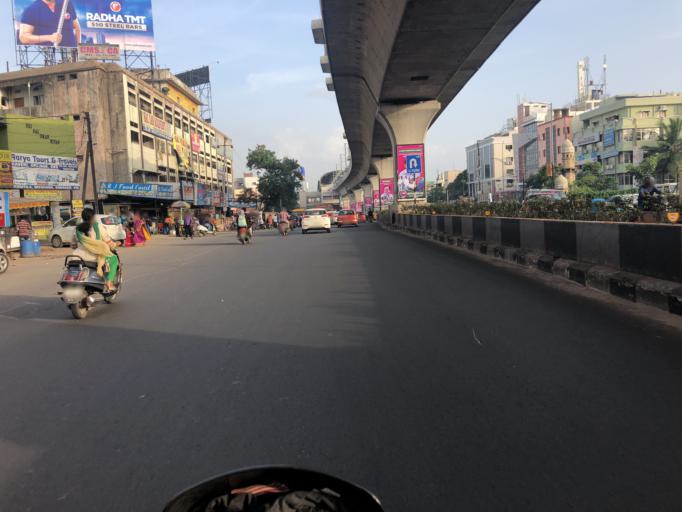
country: IN
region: Telangana
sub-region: Rangareddi
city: Kukatpalli
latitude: 17.4442
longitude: 78.4403
